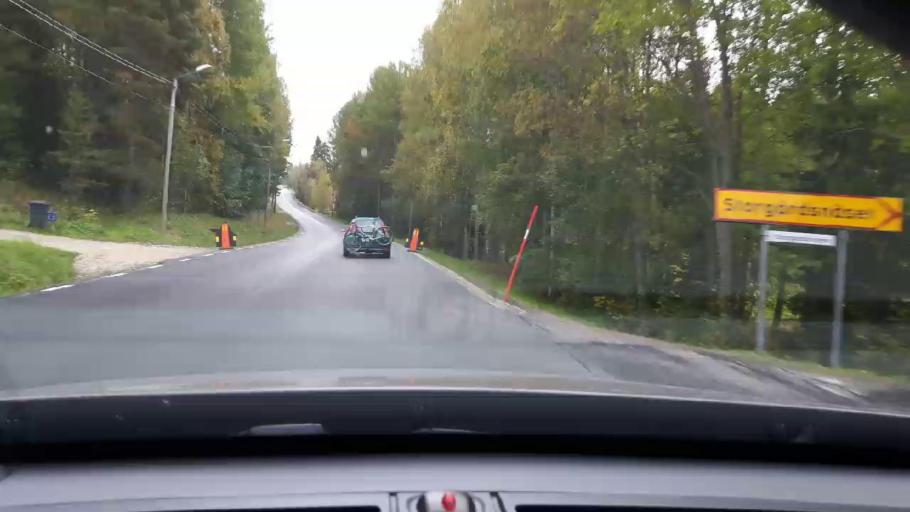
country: SE
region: Dalarna
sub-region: Ludvika Kommun
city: Ludvika
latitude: 60.2001
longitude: 15.1329
